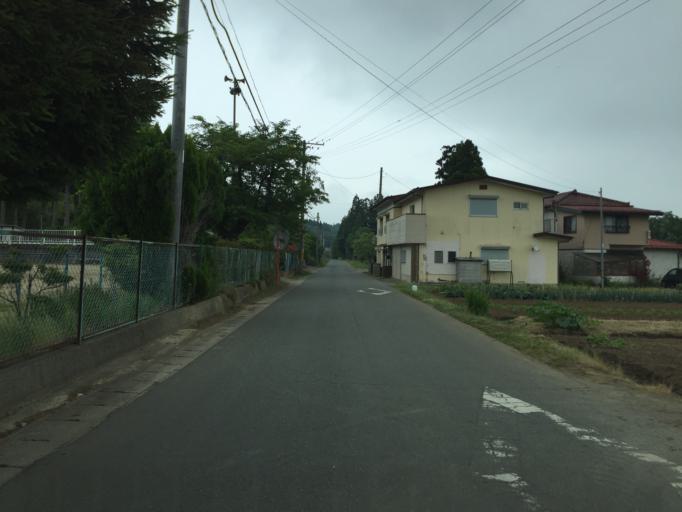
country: JP
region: Fukushima
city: Yanagawamachi-saiwaicho
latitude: 37.7690
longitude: 140.7158
